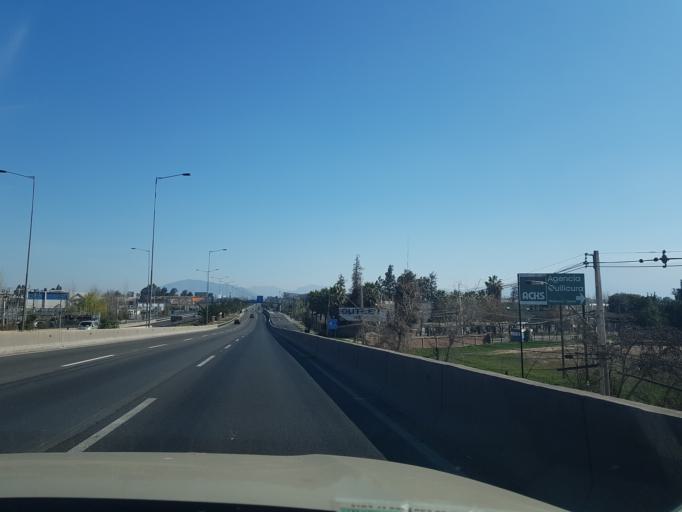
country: CL
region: Santiago Metropolitan
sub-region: Provincia de Santiago
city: Lo Prado
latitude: -33.3767
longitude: -70.7489
